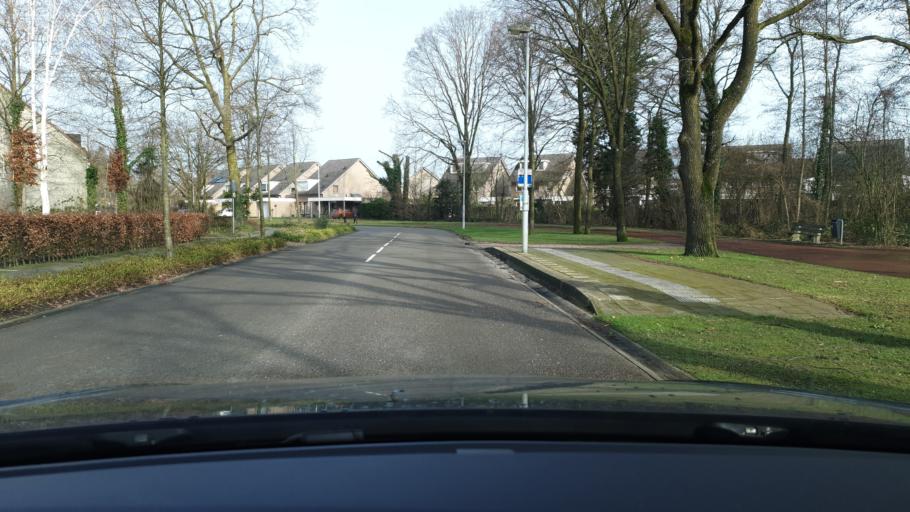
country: NL
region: North Brabant
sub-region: Gemeente Eindhoven
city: Meerhoven
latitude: 51.4756
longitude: 5.4293
